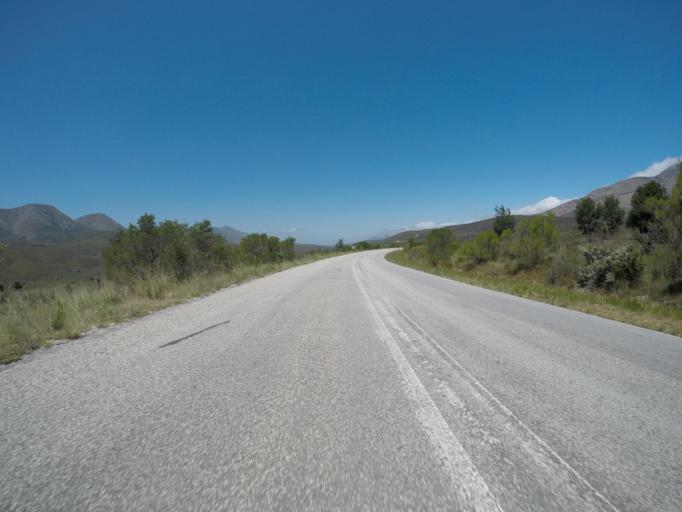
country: ZA
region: Eastern Cape
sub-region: Cacadu District Municipality
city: Kareedouw
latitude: -33.8905
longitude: 24.1000
